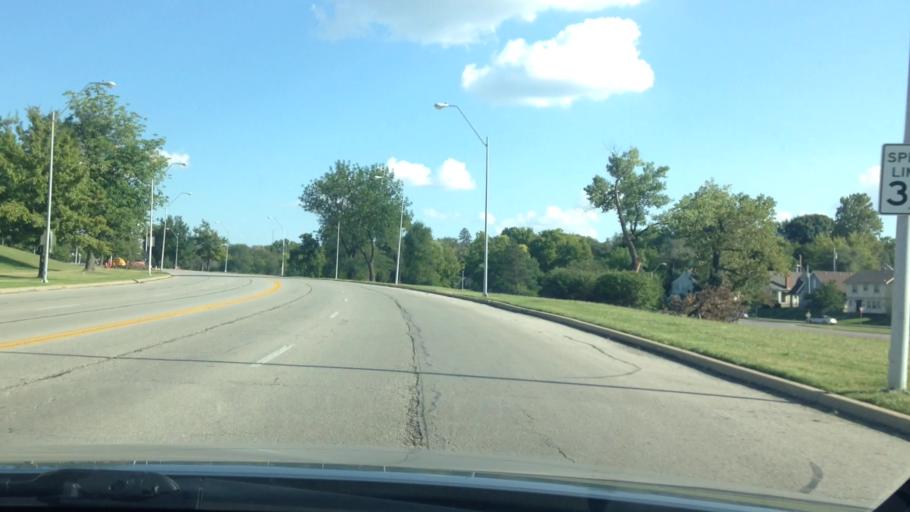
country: US
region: Kansas
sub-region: Johnson County
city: Mission Hills
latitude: 39.0094
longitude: -94.5673
